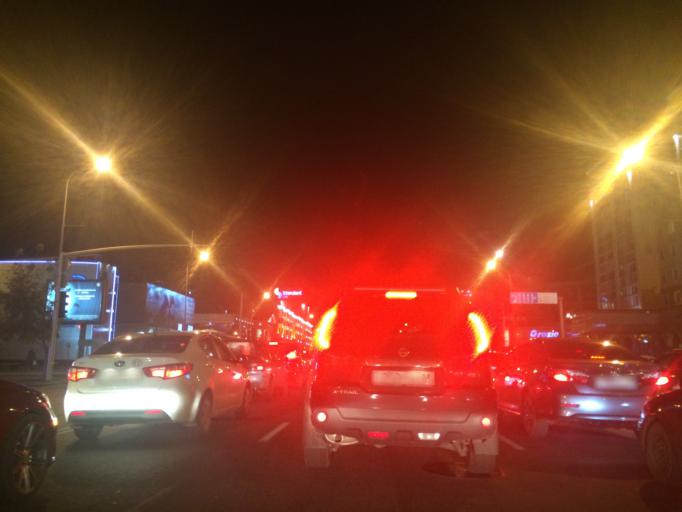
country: KZ
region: Astana Qalasy
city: Astana
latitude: 51.1618
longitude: 71.4284
